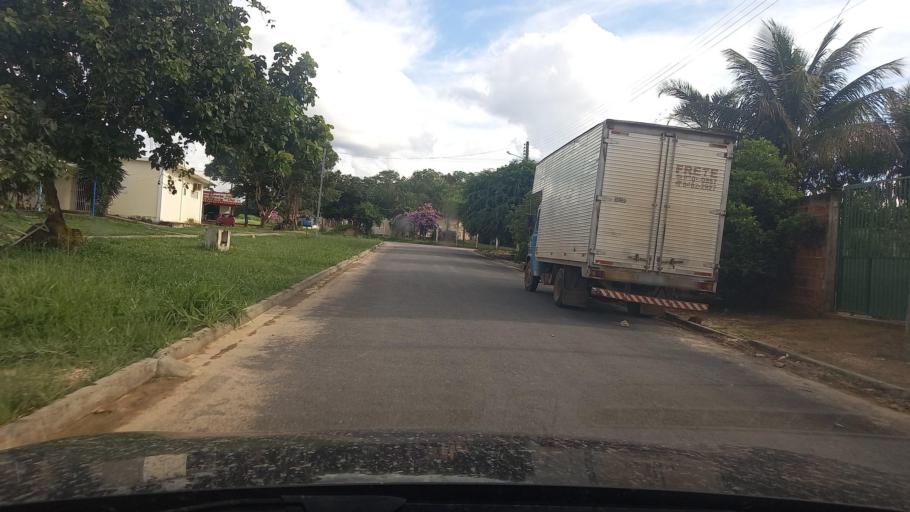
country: BR
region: Goias
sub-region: Cavalcante
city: Cavalcante
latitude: -13.7979
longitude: -47.4474
